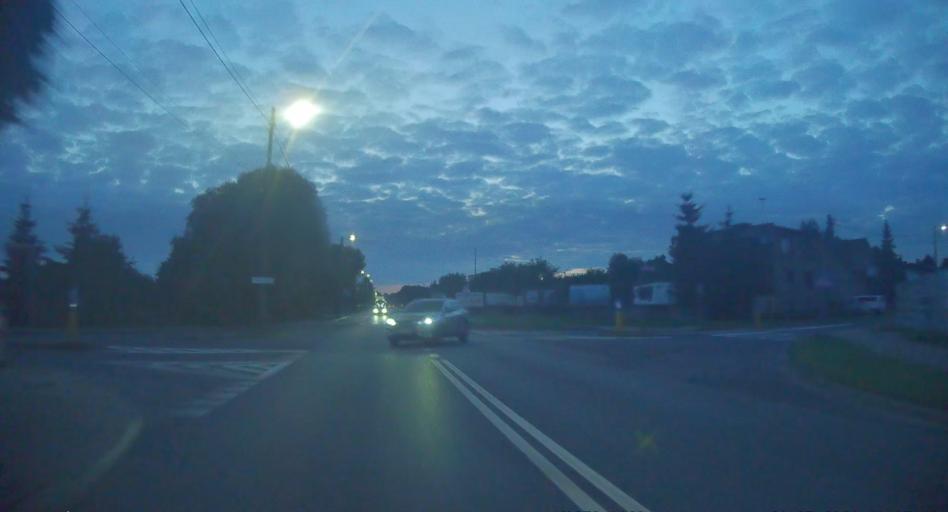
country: PL
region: Silesian Voivodeship
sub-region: Powiat klobucki
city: Klobuck
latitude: 50.9032
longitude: 18.9296
